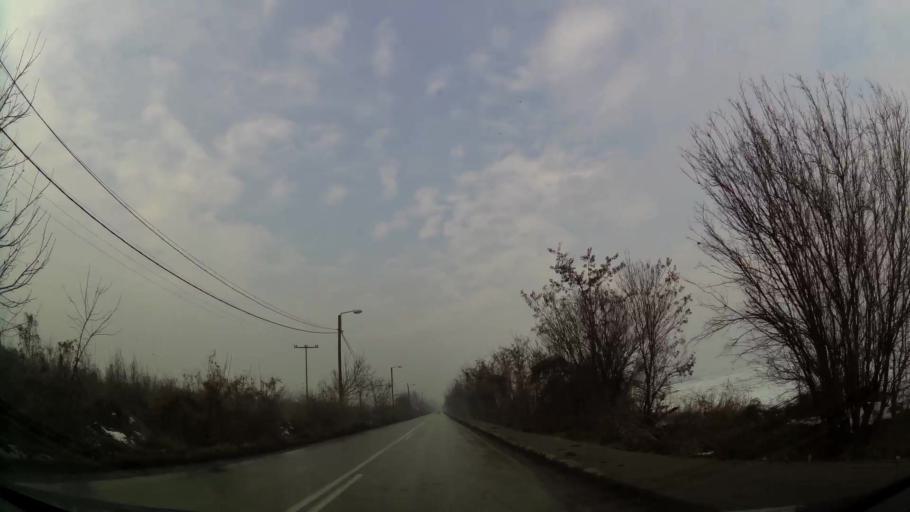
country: MK
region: Ilinden
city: Jurumleri
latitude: 41.9839
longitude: 21.5221
